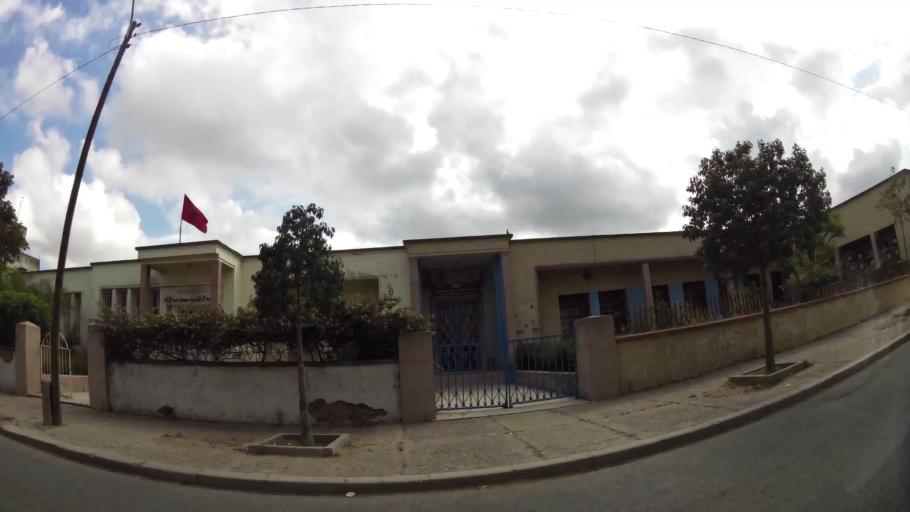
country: MA
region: Gharb-Chrarda-Beni Hssen
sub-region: Kenitra Province
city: Kenitra
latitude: 34.2614
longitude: -6.5681
